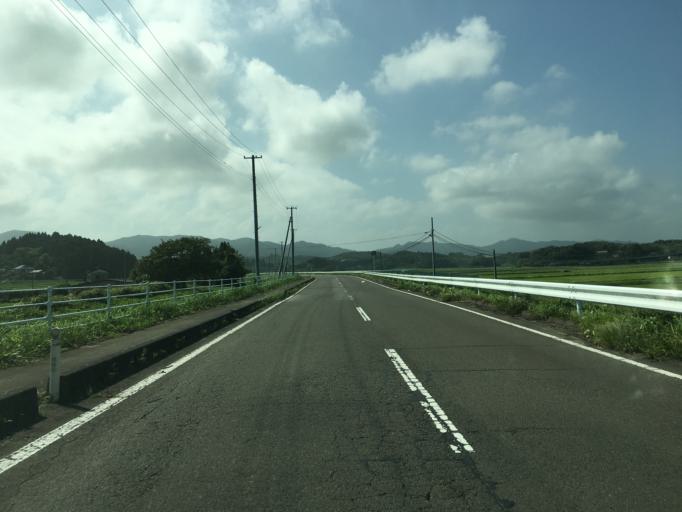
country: JP
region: Miyagi
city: Marumori
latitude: 37.8887
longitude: 140.9063
